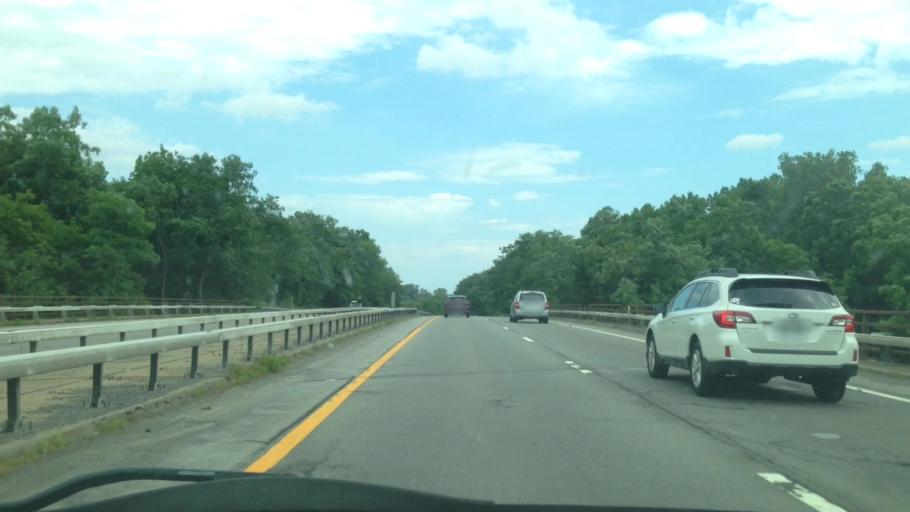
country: US
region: New York
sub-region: Monroe County
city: Fairport
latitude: 43.0641
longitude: -77.4719
